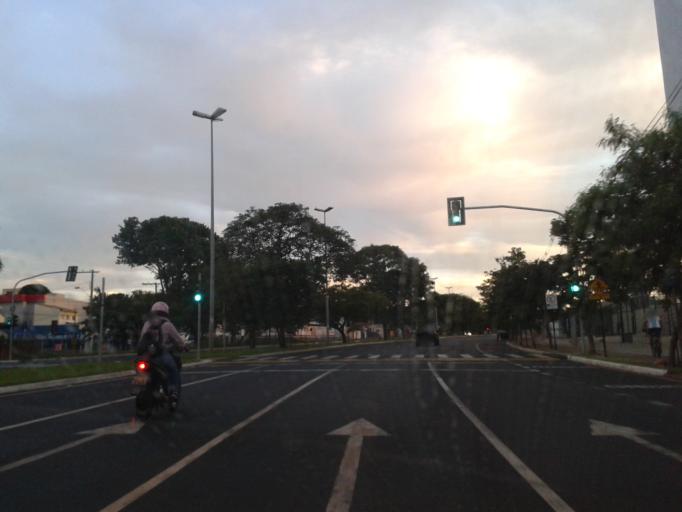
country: BR
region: Minas Gerais
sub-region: Uberlandia
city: Uberlandia
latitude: -18.8986
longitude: -48.2577
